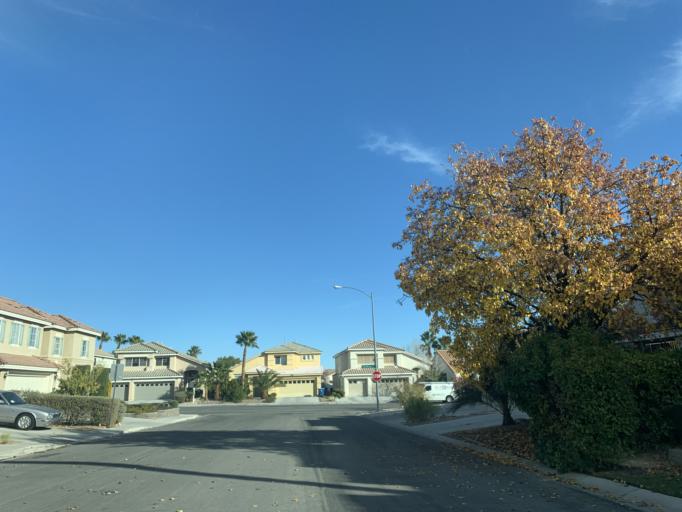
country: US
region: Nevada
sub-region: Clark County
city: Summerlin South
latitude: 36.1272
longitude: -115.2999
